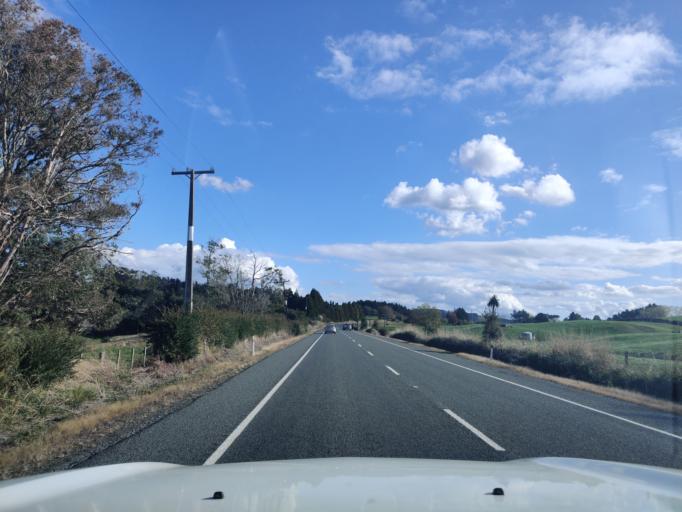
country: NZ
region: Waikato
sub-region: Hauraki District
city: Ngatea
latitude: -37.2883
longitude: 175.3873
